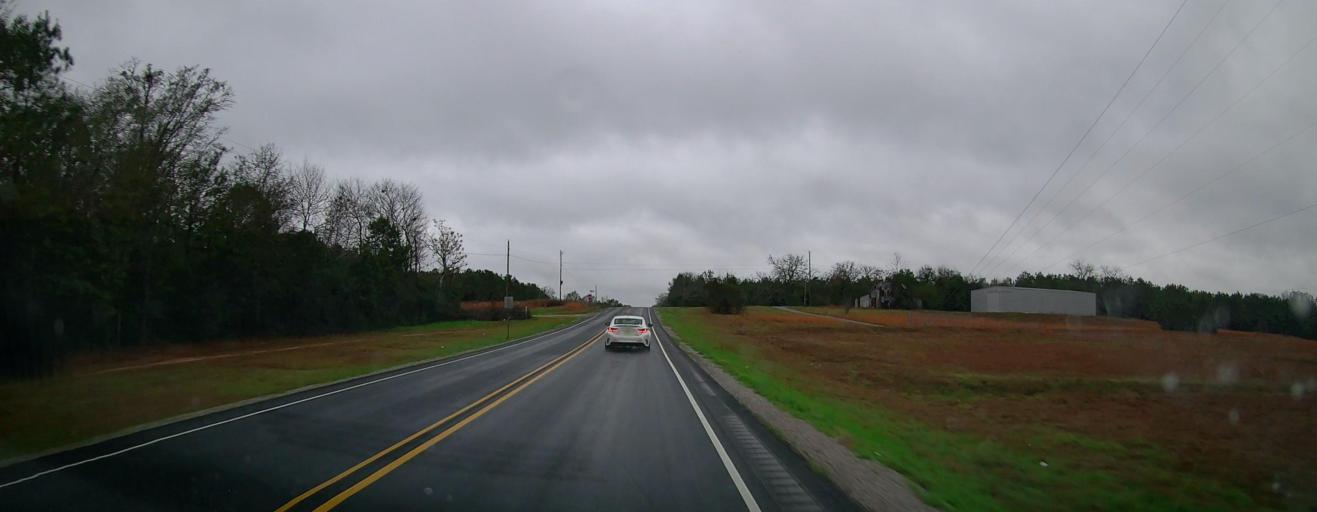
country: US
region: Alabama
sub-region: Chilton County
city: Clanton
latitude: 32.6539
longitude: -86.7674
